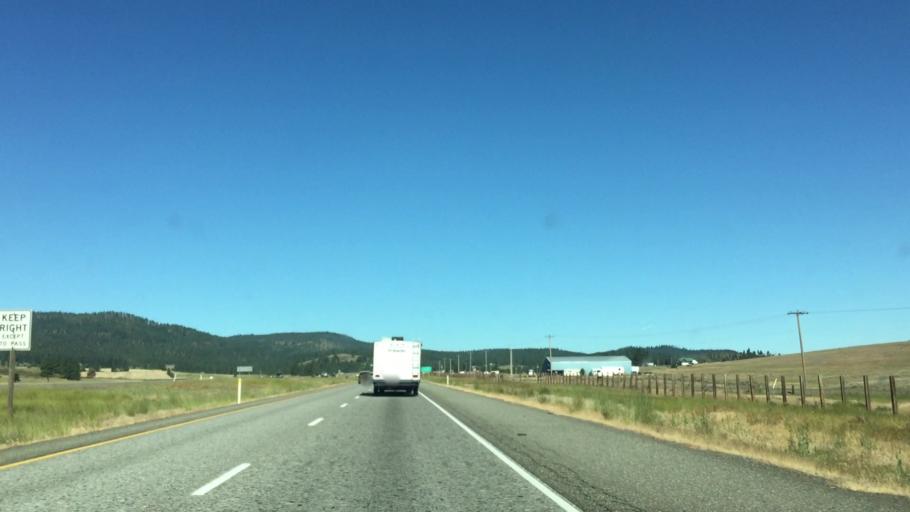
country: US
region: Washington
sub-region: Kittitas County
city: Cle Elum
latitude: 47.1089
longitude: -120.7706
